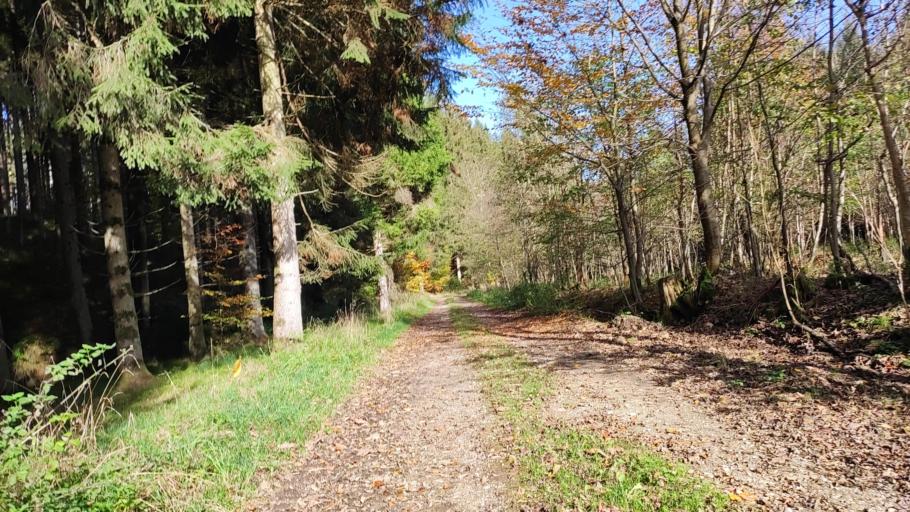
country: DE
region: Bavaria
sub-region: Swabia
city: Ziemetshausen
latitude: 48.3440
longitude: 10.5349
